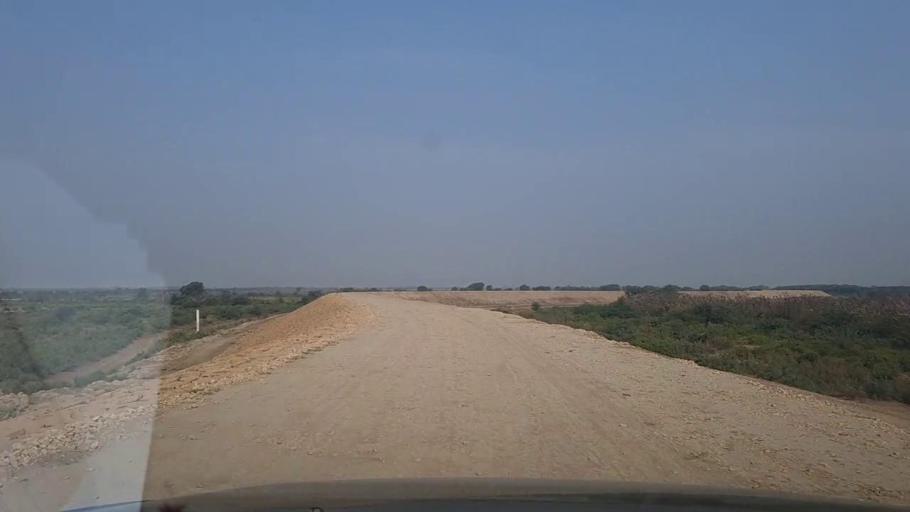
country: PK
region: Sindh
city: Bulri
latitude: 24.9666
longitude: 68.2908
